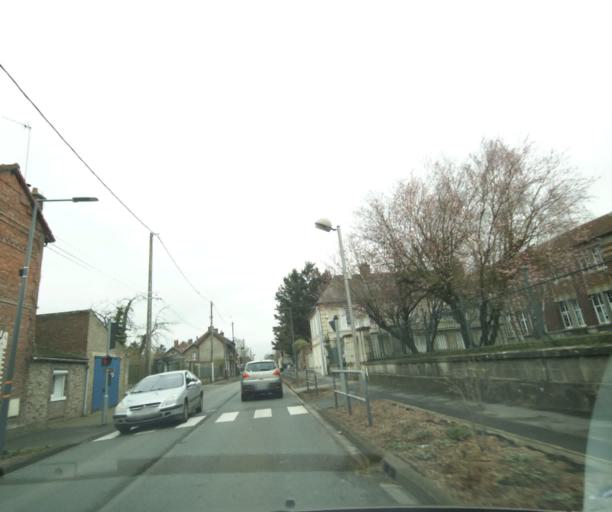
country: FR
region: Picardie
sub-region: Departement de l'Oise
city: Noyon
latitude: 49.5740
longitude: 3.0131
